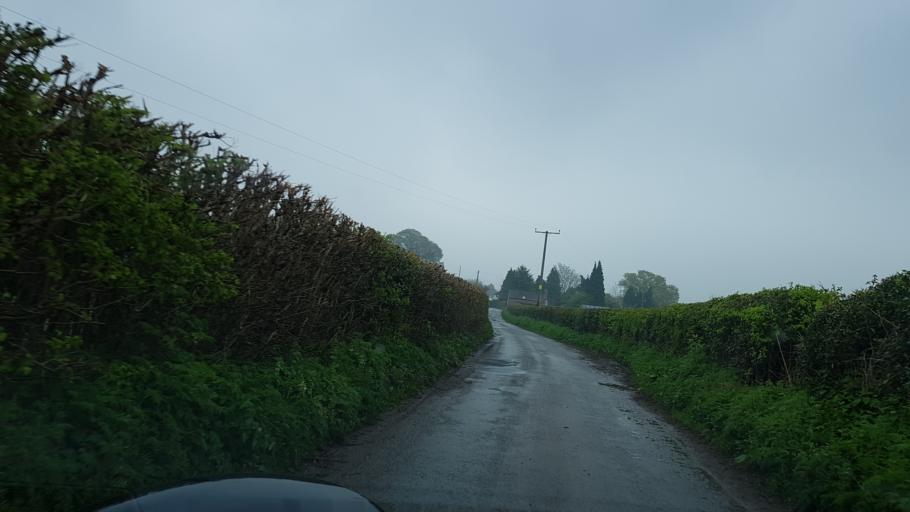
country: GB
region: England
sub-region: Herefordshire
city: Brockhampton
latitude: 51.9802
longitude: -2.6031
